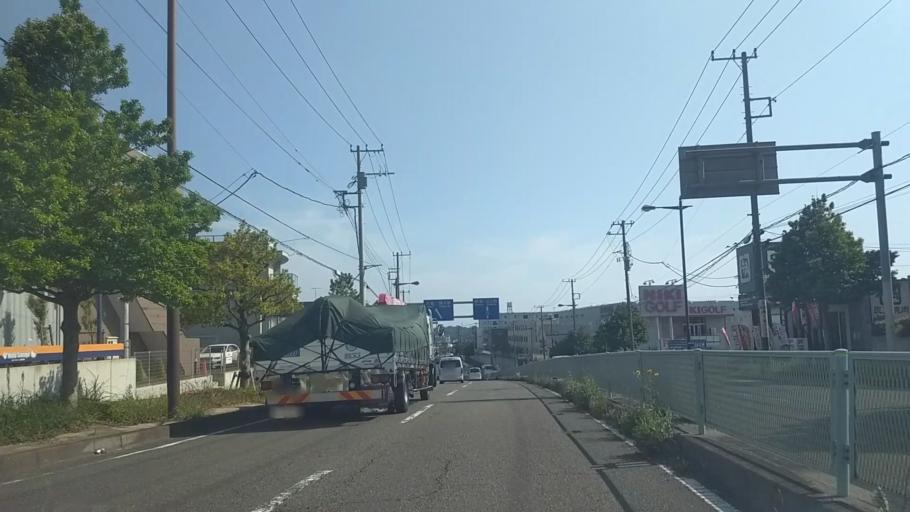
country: JP
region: Kanagawa
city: Fujisawa
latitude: 35.3519
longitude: 139.5010
